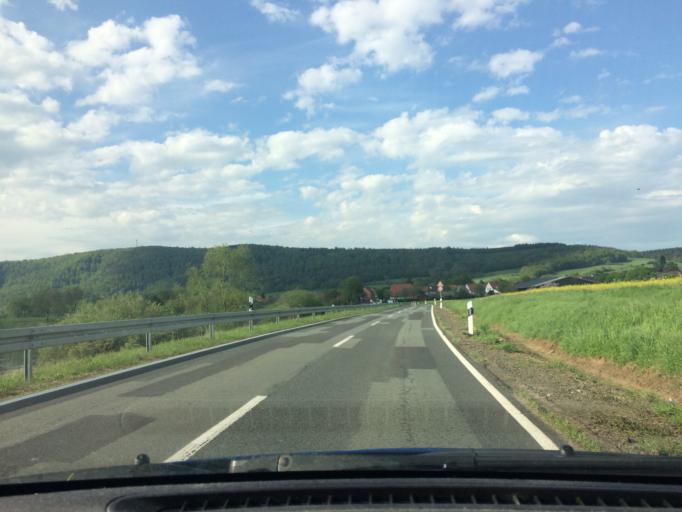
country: DE
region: Lower Saxony
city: Bodenfelde
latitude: 51.5837
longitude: 9.5942
